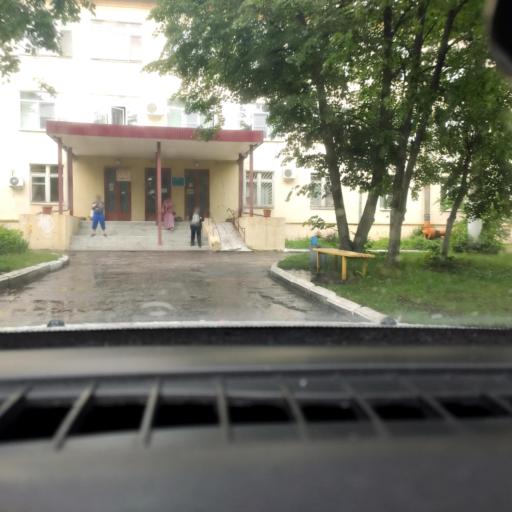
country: RU
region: Voronezj
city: Somovo
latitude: 51.7498
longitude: 39.3797
